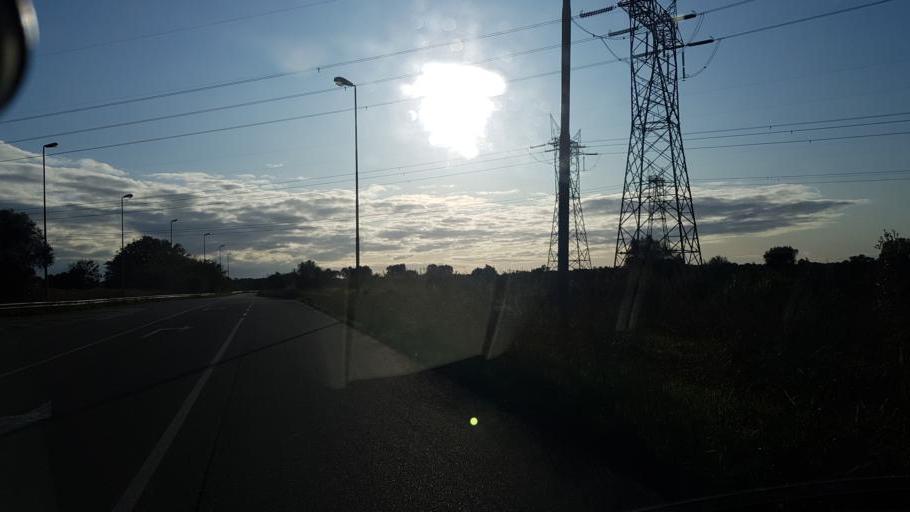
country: IT
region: Apulia
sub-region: Provincia di Brindisi
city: San Pietro Vernotico
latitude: 40.5557
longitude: 18.0287
